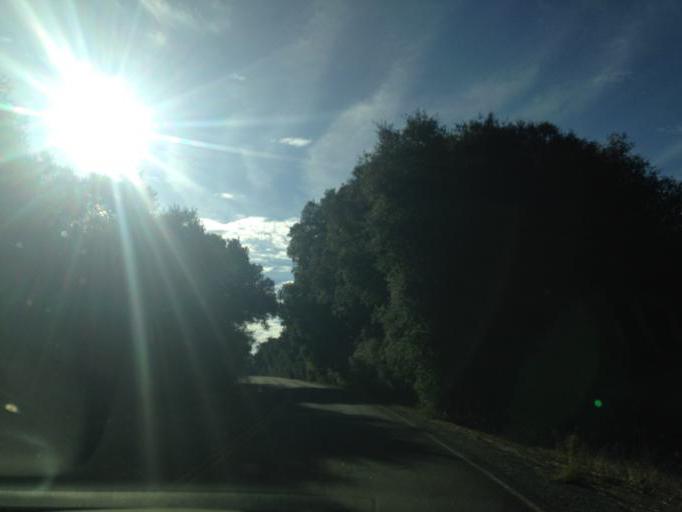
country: US
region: California
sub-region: San Diego County
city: Ramona
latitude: 33.2297
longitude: -116.7587
